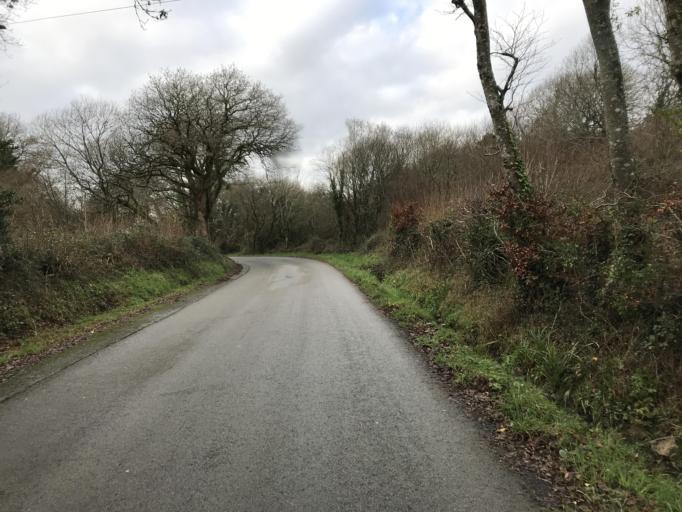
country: FR
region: Brittany
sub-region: Departement du Finistere
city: Plougastel-Daoulas
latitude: 48.3735
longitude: -4.3532
